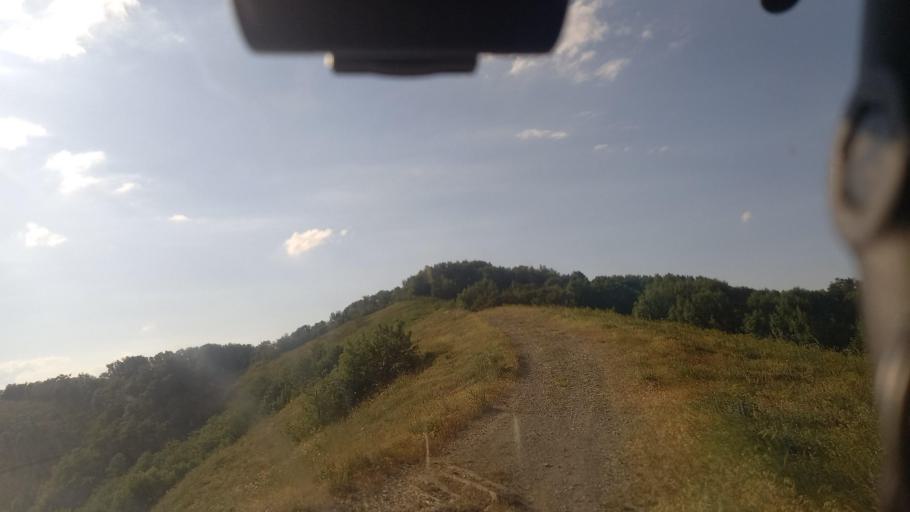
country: RU
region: Krasnodarskiy
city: Gelendzhik
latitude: 44.6171
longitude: 38.1948
